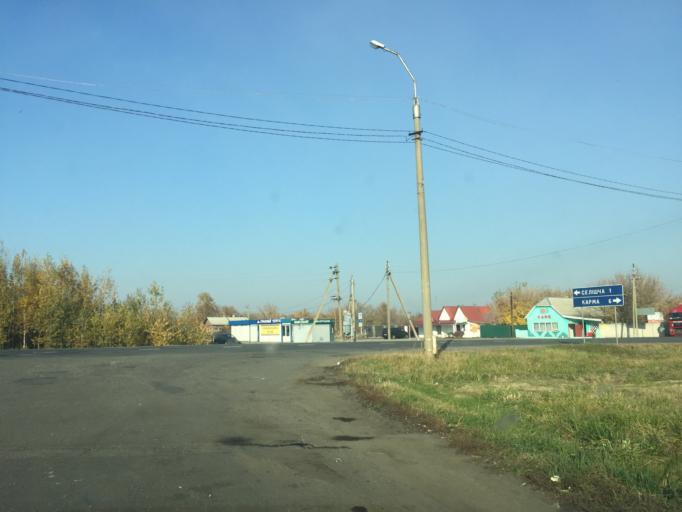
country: BY
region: Gomel
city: Dobrush
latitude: 52.3880
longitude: 31.4651
